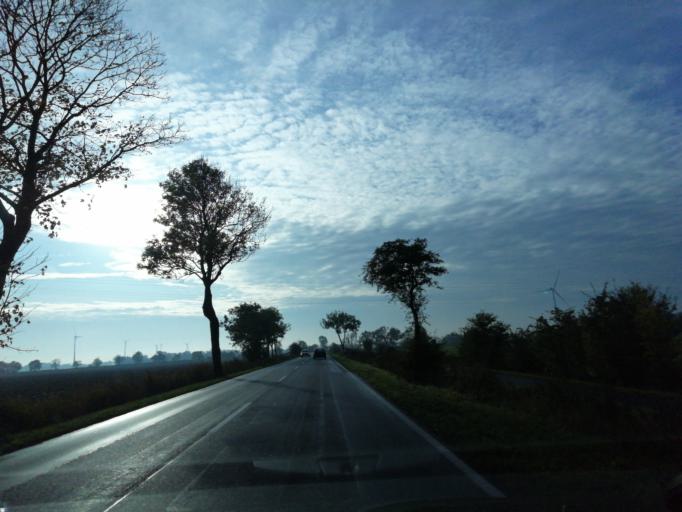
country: DE
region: Lower Saxony
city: Fedderwarden
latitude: 53.6181
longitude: 8.0367
